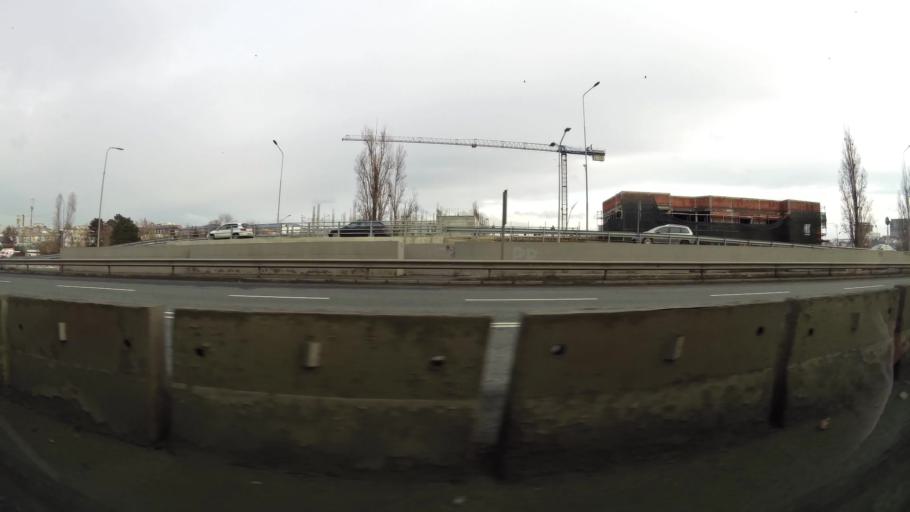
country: XK
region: Pristina
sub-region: Komuna e Prishtines
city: Pristina
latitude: 42.6434
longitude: 21.1563
